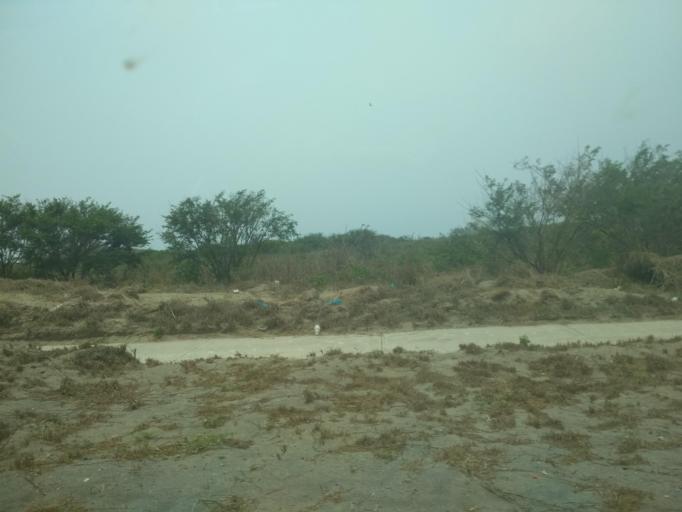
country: MX
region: Veracruz
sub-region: Alvarado
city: Playa de la Libertad
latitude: 19.0594
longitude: -96.0709
